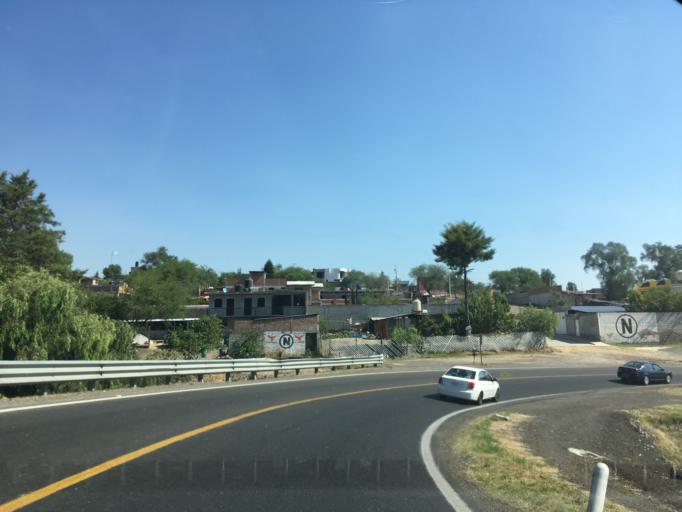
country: MX
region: Michoacan
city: Charo
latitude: 19.7505
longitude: -101.0497
